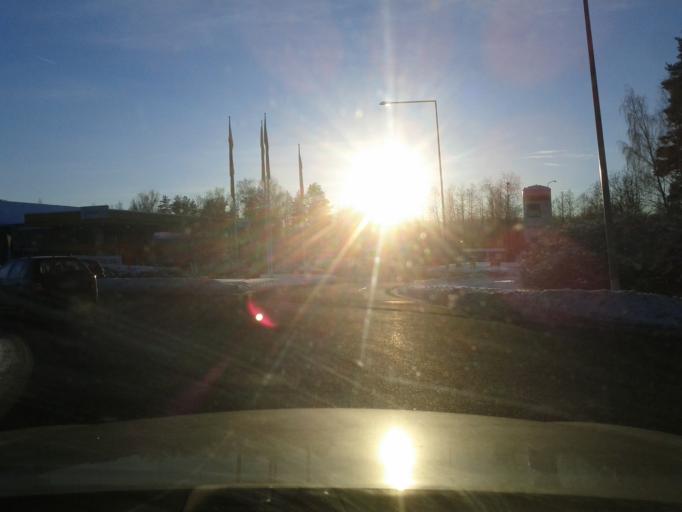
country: SE
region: Dalarna
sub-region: Faluns Kommun
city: Falun
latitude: 60.6258
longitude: 15.6115
